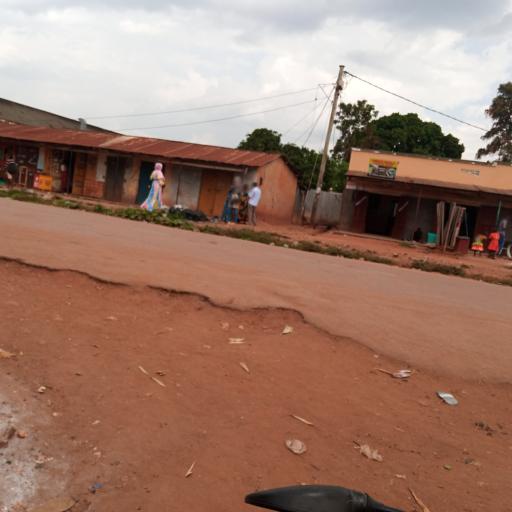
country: UG
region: Eastern Region
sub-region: Mbale District
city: Mbale
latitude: 1.0987
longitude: 34.1761
